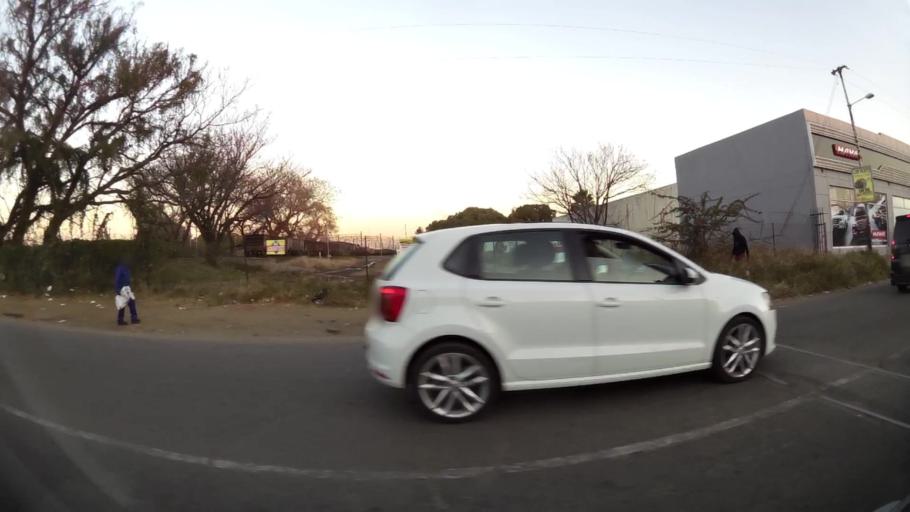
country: ZA
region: North-West
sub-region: Bojanala Platinum District Municipality
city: Rustenburg
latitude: -25.6641
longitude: 27.2496
